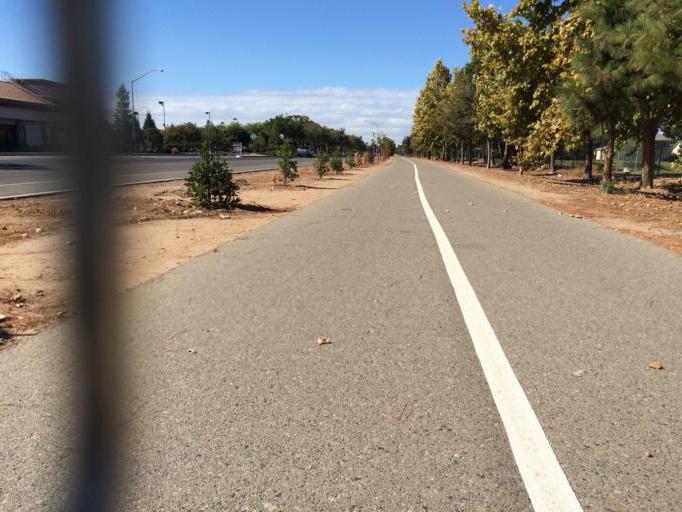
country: US
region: California
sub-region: Fresno County
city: Clovis
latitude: 36.8668
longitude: -119.7400
